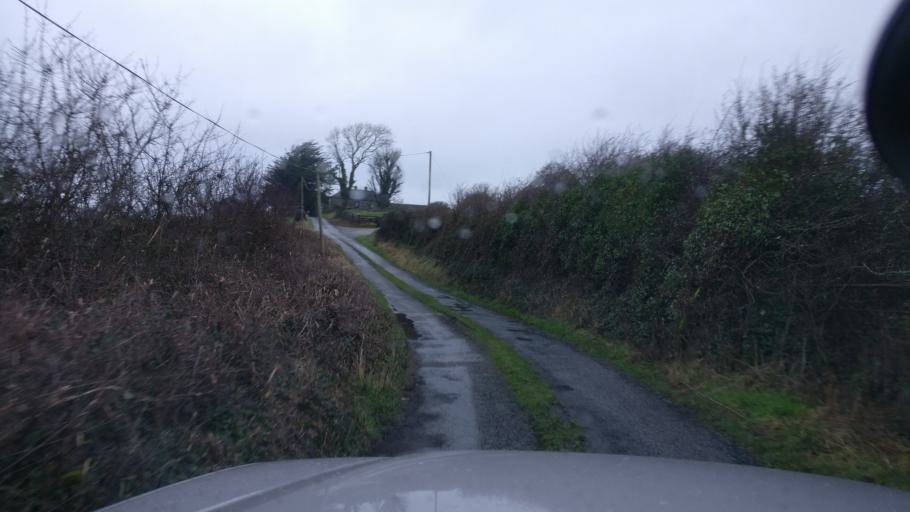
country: IE
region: Connaught
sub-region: County Galway
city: Loughrea
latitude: 53.1626
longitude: -8.6103
